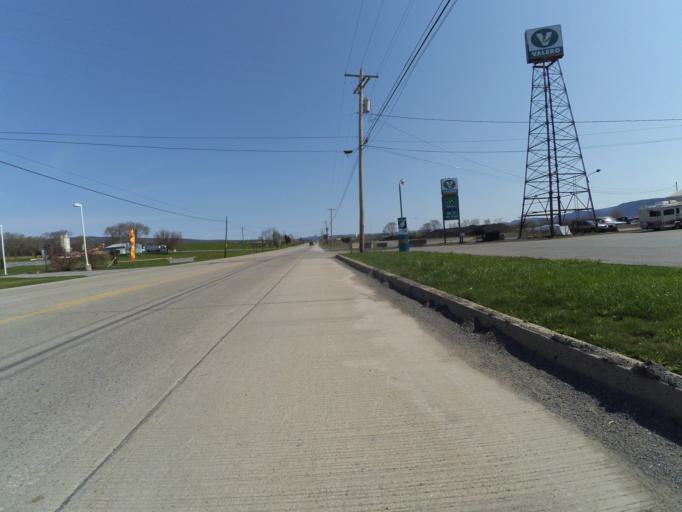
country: US
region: Pennsylvania
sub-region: Clinton County
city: Mill Hall
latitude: 41.0248
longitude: -77.5240
